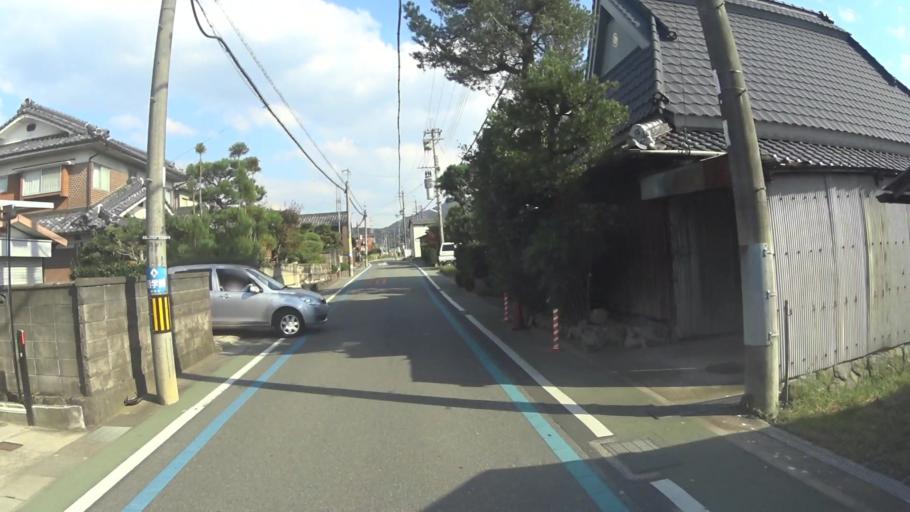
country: JP
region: Kyoto
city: Kameoka
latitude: 35.0002
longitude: 135.6127
